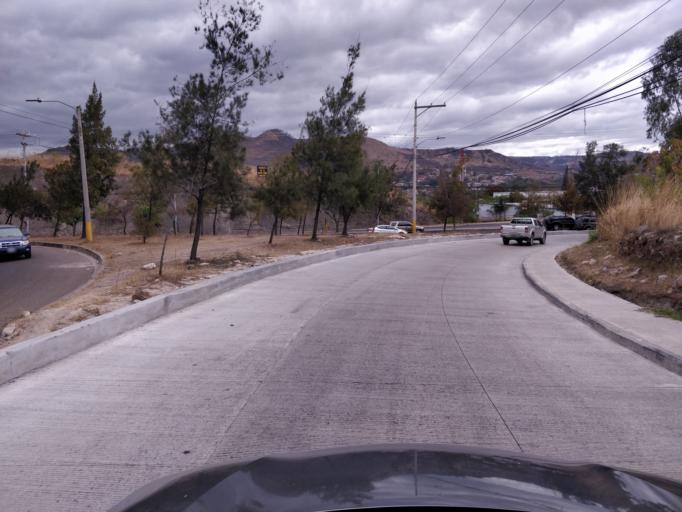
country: HN
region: Francisco Morazan
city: Tegucigalpa
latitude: 14.0497
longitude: -87.2127
